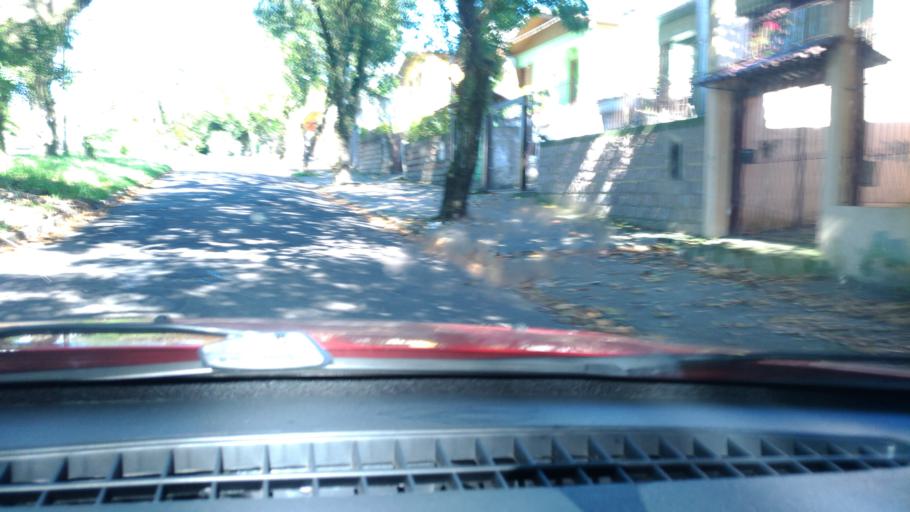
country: BR
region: Rio Grande do Sul
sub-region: Cachoeirinha
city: Cachoeirinha
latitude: -30.0325
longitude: -51.1288
